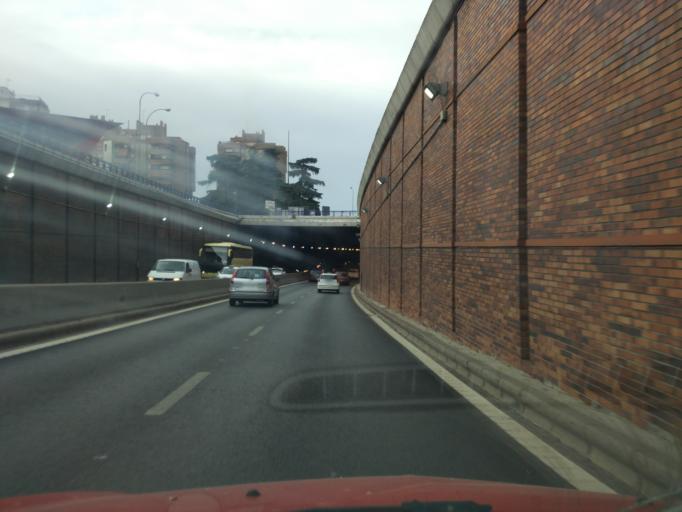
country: ES
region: Madrid
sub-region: Provincia de Madrid
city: Carabanchel
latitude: 40.3840
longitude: -3.7179
